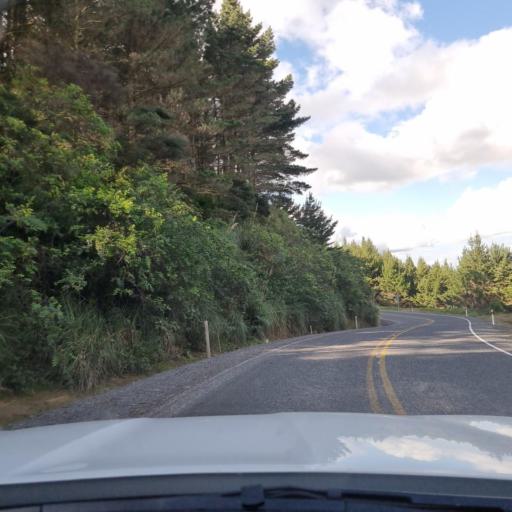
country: NZ
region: Northland
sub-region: Kaipara District
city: Dargaville
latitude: -36.2445
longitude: 174.0446
